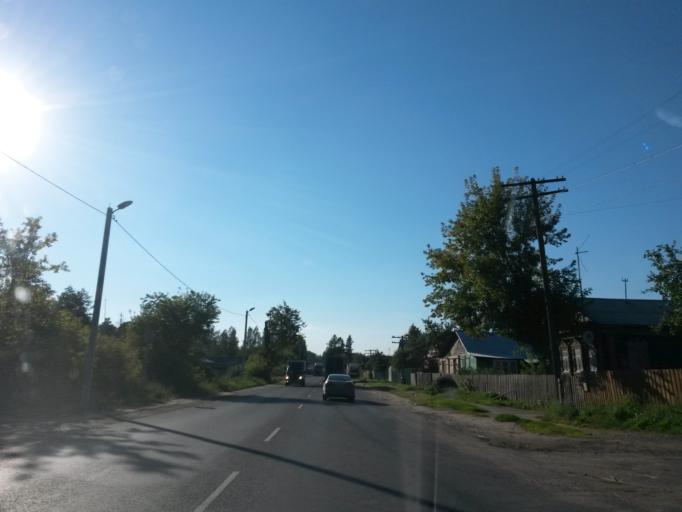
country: RU
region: Ivanovo
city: Novo-Talitsy
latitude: 57.0650
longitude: 40.7058
